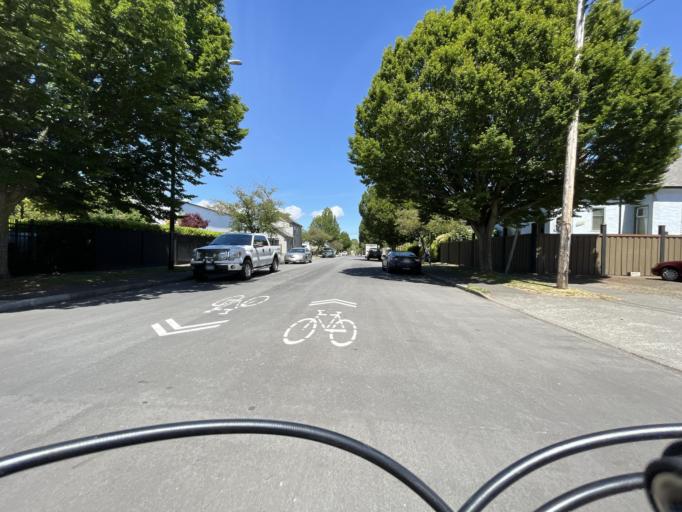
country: CA
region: British Columbia
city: Victoria
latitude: 48.4290
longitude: -123.3560
